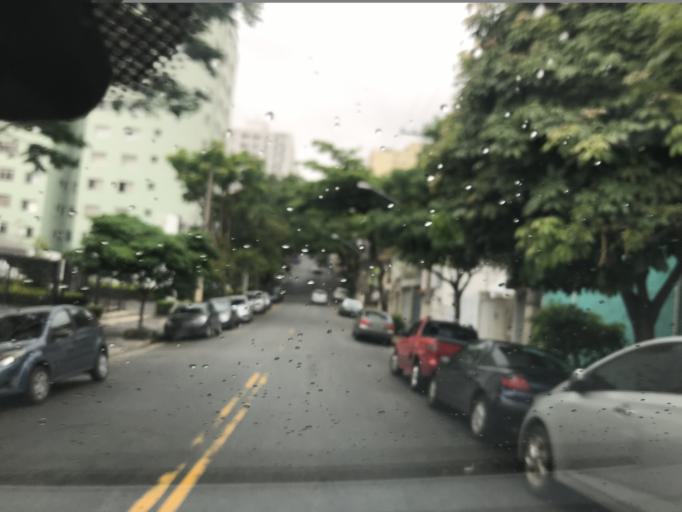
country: BR
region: Sao Paulo
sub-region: Sao Paulo
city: Sao Paulo
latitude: -23.5392
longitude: -46.6761
